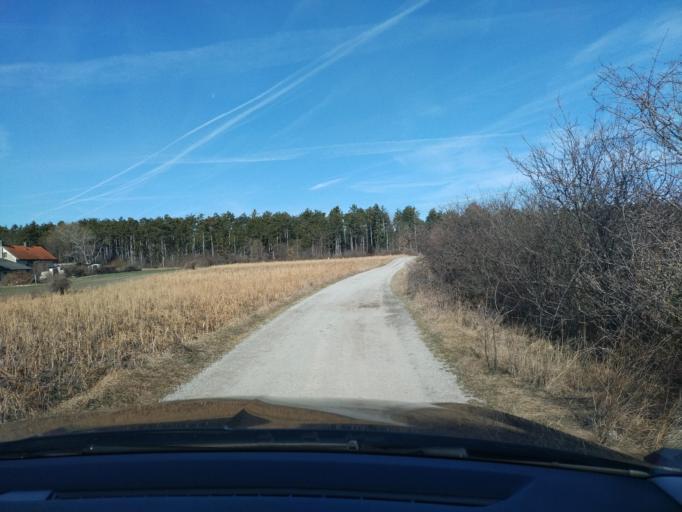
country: AT
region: Lower Austria
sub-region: Politischer Bezirk Neunkirchen
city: Breitenau
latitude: 47.7430
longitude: 16.1659
